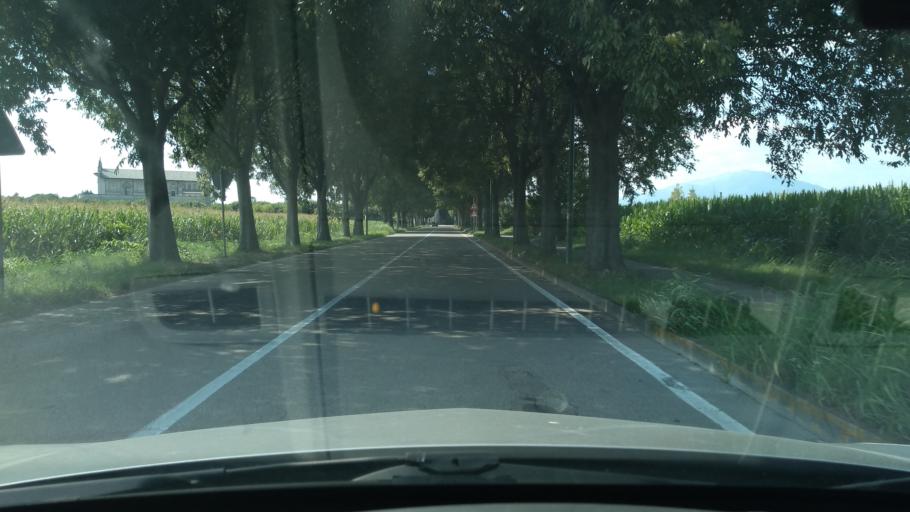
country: IT
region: Lombardy
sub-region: Provincia di Bergamo
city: Stezzano
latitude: 45.6595
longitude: 9.6431
